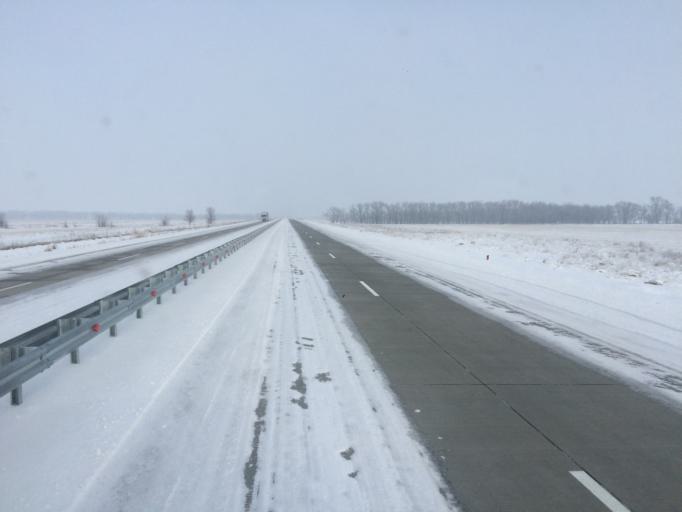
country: KG
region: Chuy
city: Sokuluk
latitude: 43.2991
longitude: 74.2507
